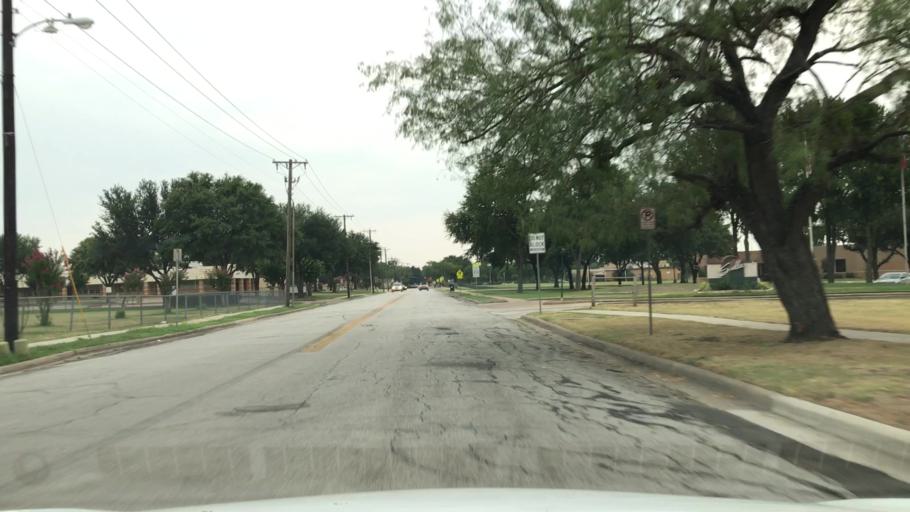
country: US
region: Texas
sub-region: Dallas County
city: Carrollton
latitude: 32.9580
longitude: -96.8957
